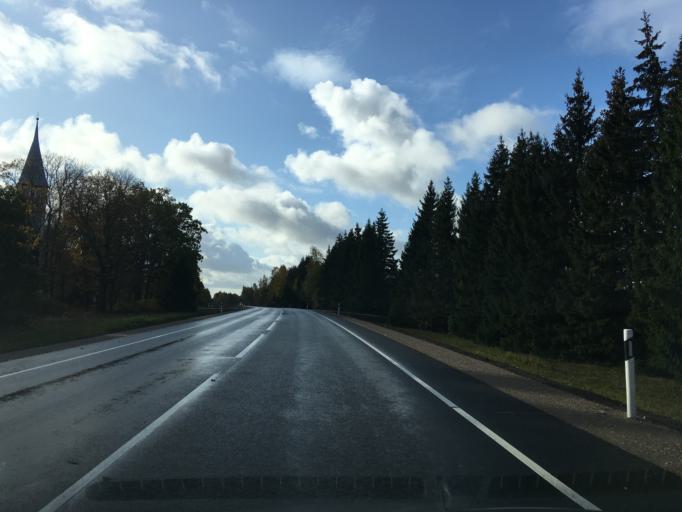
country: EE
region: Laeaene
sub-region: Lihula vald
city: Lihula
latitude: 58.6377
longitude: 23.6902
